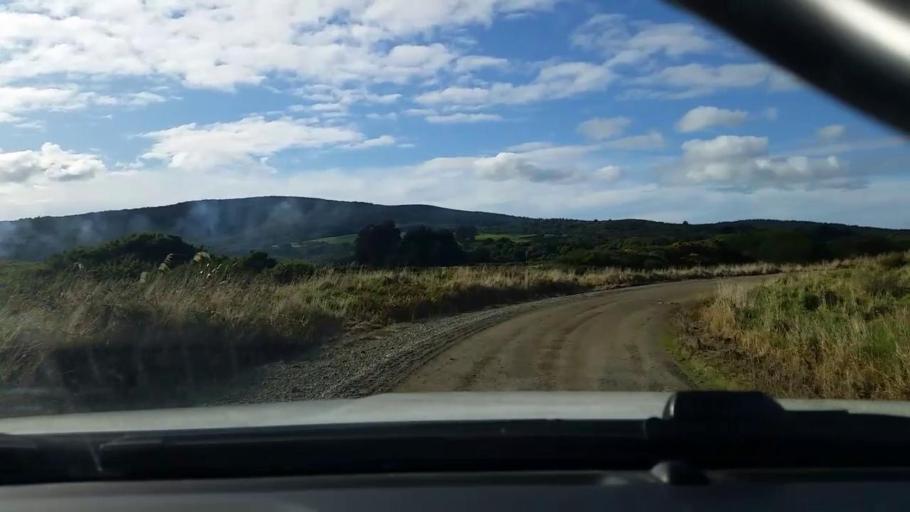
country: NZ
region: Southland
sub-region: Southland District
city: Riverton
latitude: -46.3329
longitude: 167.8188
